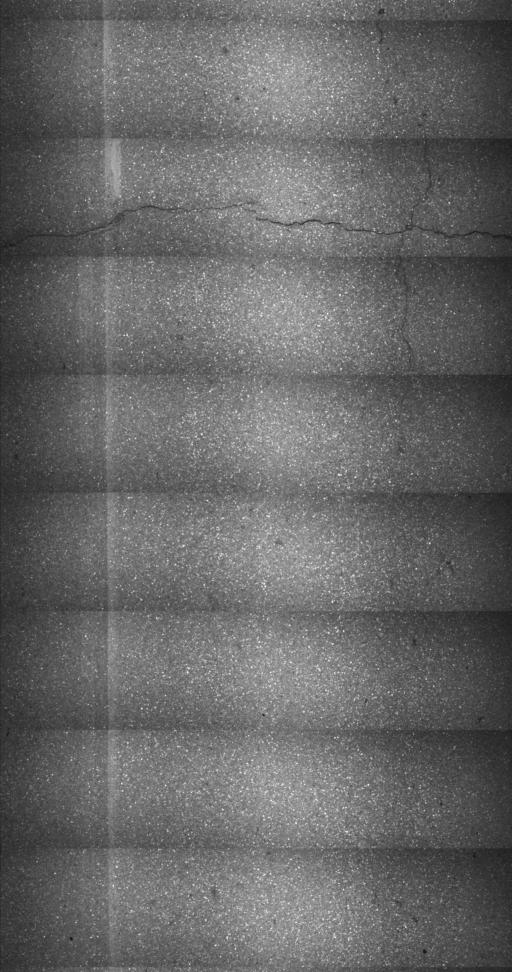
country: US
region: Vermont
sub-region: Washington County
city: Waterbury
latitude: 44.1963
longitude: -72.8920
